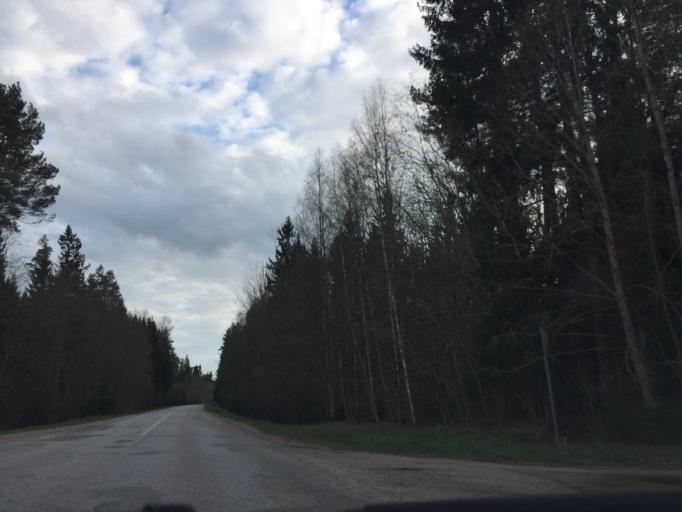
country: LV
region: Aluksnes Rajons
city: Aluksne
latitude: 57.3045
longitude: 27.0702
